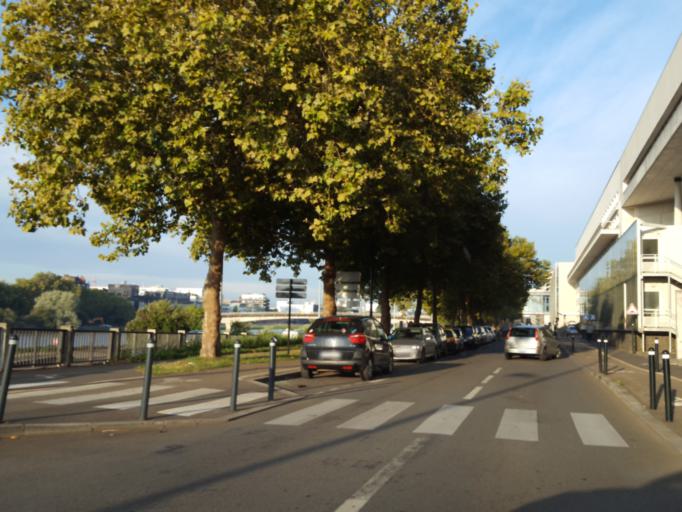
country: FR
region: Pays de la Loire
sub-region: Departement de la Loire-Atlantique
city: Nantes
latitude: 47.2088
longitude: -1.5504
